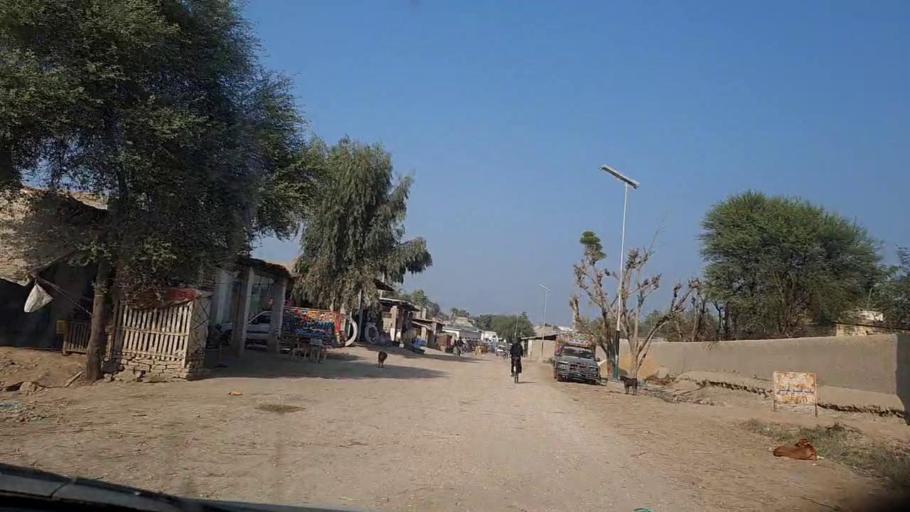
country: PK
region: Sindh
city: Moro
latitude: 26.7894
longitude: 67.9398
